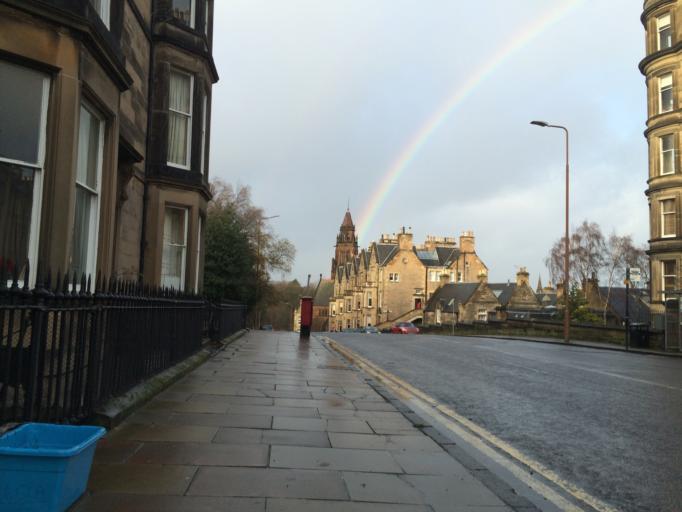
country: GB
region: Scotland
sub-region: Edinburgh
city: Edinburgh
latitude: 55.9499
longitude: -3.2193
